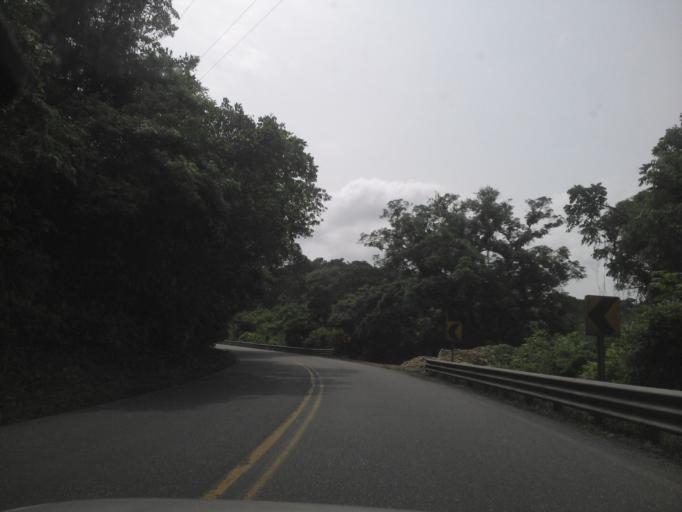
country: MX
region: Veracruz
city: Gutierrez Zamora
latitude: 20.4617
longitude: -97.1357
